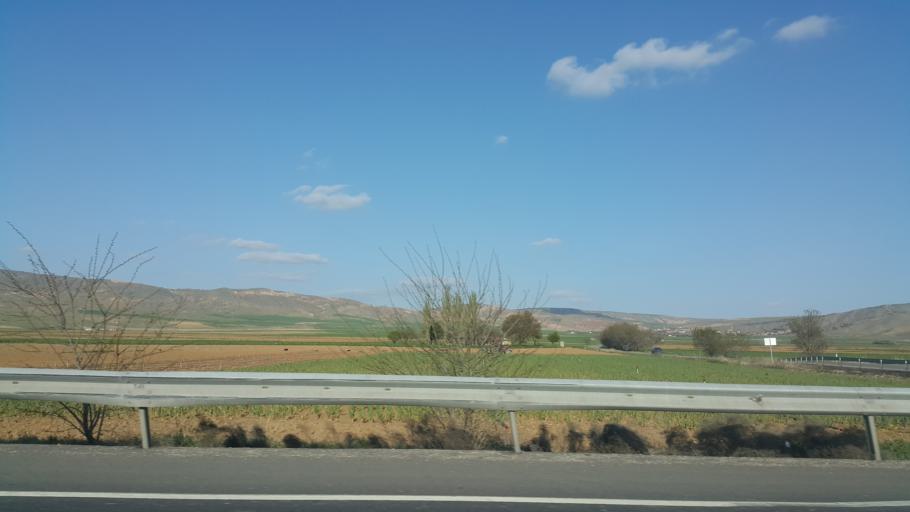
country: TR
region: Ankara
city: Sereflikochisar
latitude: 38.8646
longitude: 33.5889
